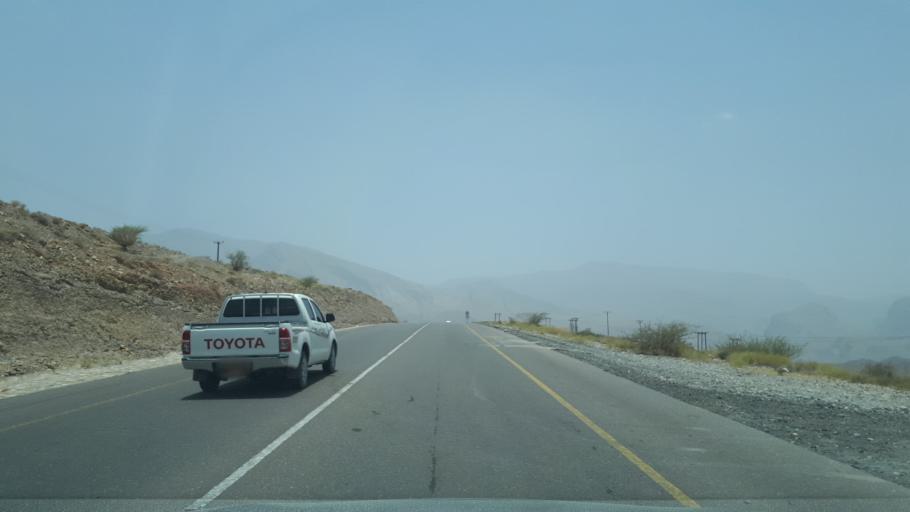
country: OM
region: Al Batinah
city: Rustaq
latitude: 23.3929
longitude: 57.2348
